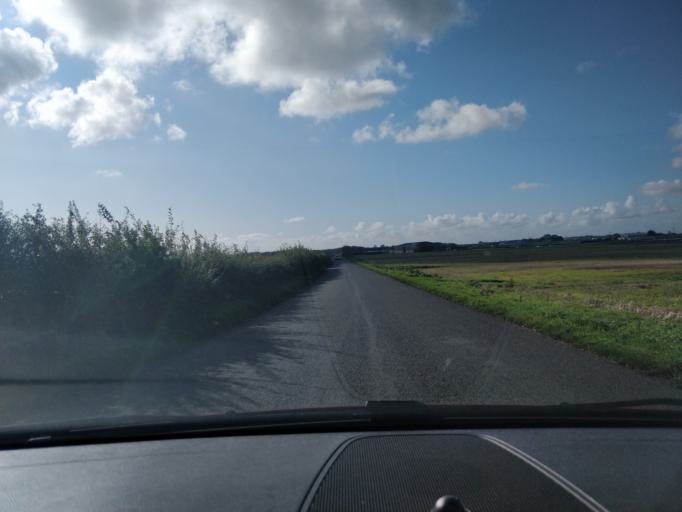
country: GB
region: England
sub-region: Lancashire
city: Tarleton
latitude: 53.6757
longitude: -2.8585
